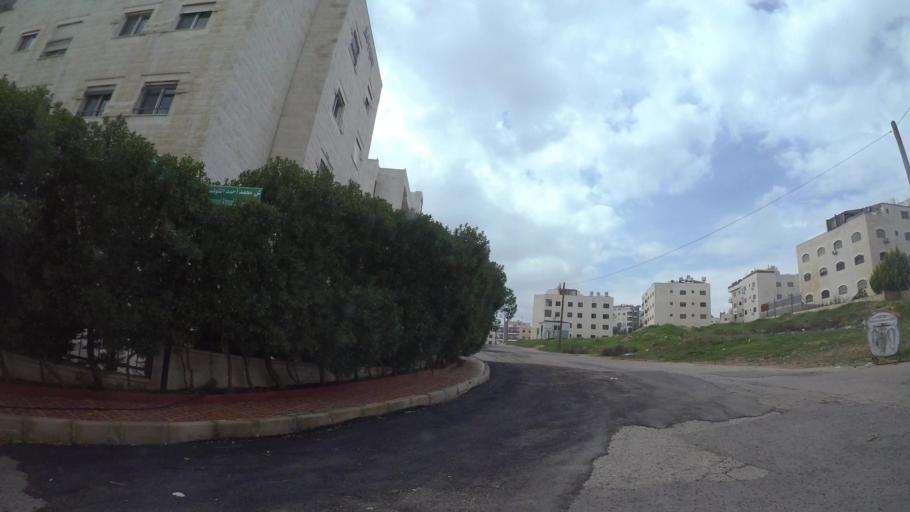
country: JO
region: Amman
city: Umm as Summaq
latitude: 31.9099
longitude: 35.8535
